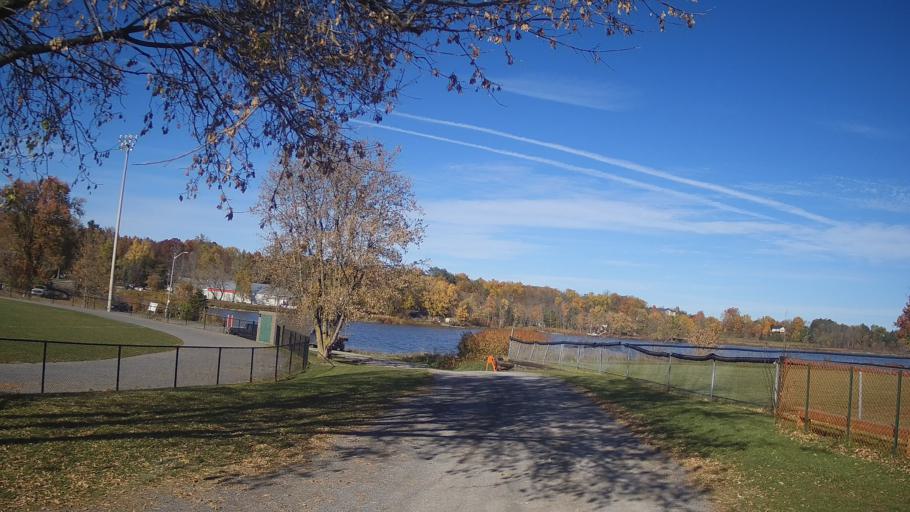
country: CA
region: Ontario
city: Kingston
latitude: 44.4106
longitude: -76.5930
